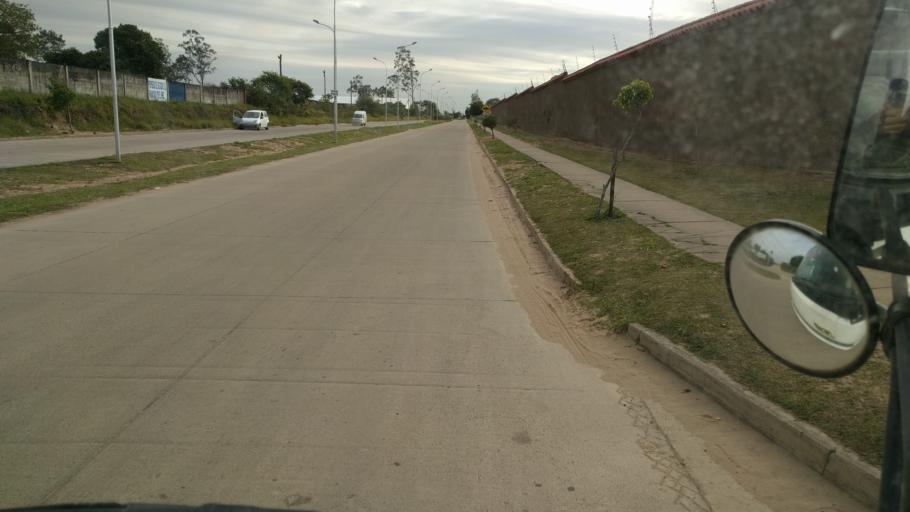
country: BO
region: Santa Cruz
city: Santa Cruz de la Sierra
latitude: -17.6832
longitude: -63.1543
